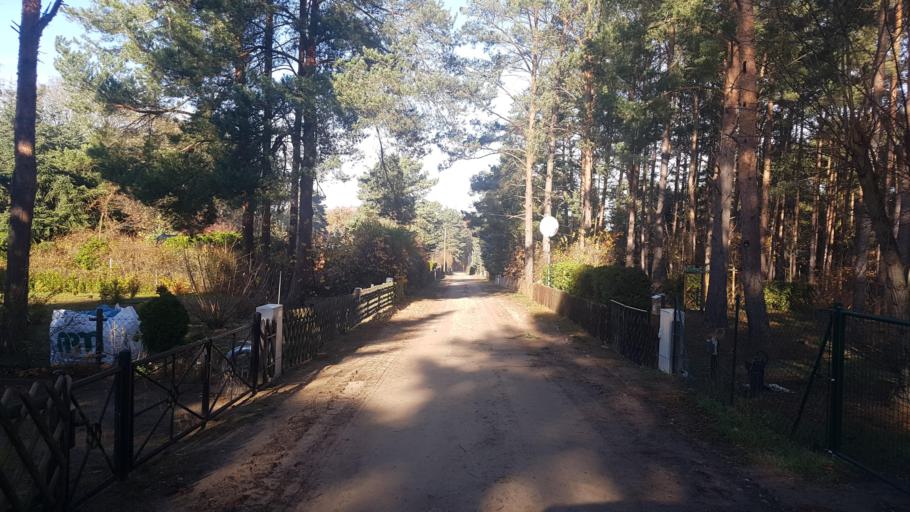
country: DE
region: Brandenburg
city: Niemegk
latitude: 52.0715
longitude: 12.7055
